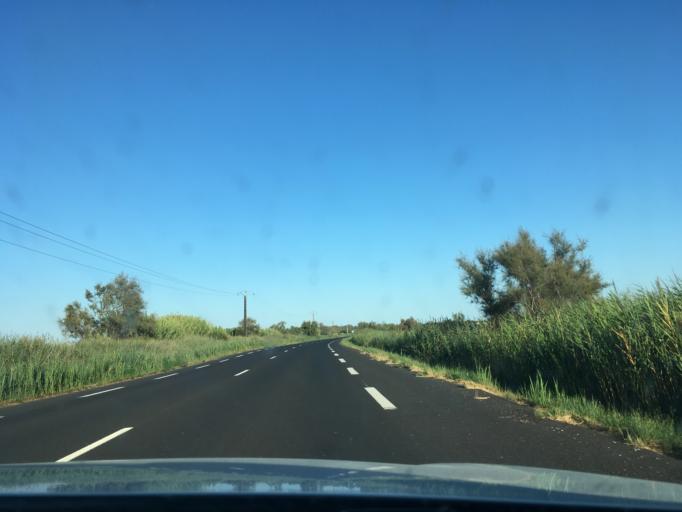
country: FR
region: Provence-Alpes-Cote d'Azur
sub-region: Departement des Bouches-du-Rhone
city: Saintes-Maries-de-la-Mer
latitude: 43.5519
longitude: 4.3340
